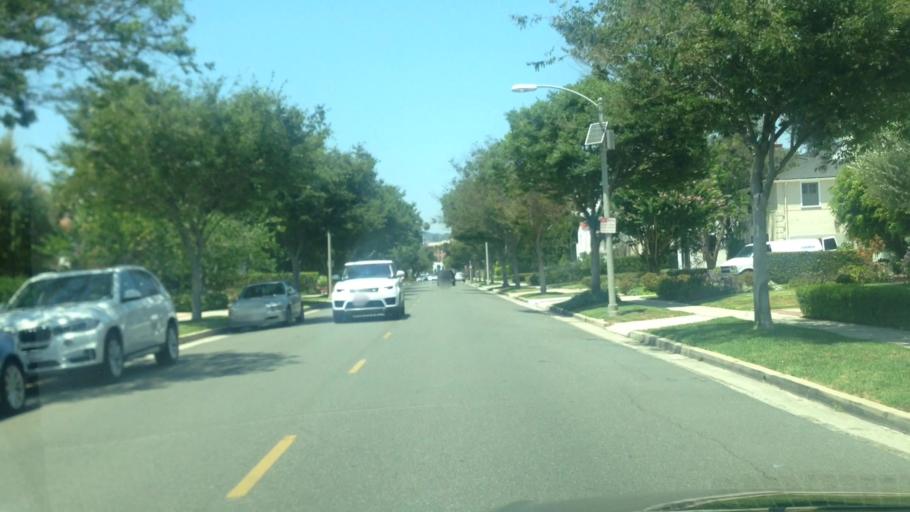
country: US
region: California
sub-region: Los Angeles County
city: Beverly Hills
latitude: 34.0630
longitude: -118.4057
